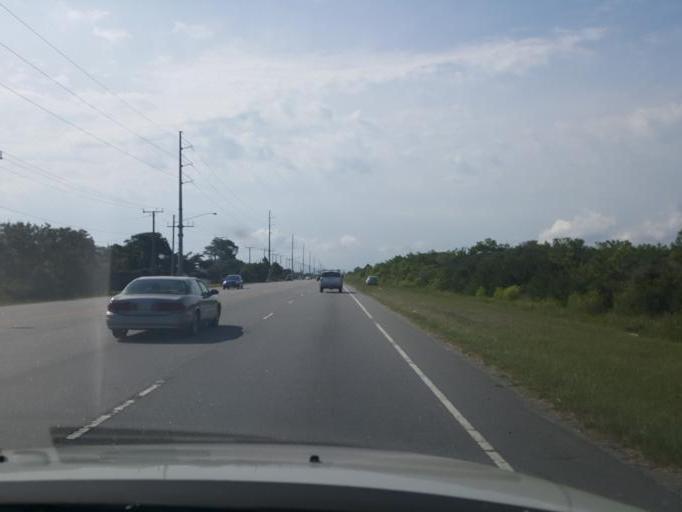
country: US
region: North Carolina
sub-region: Dare County
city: Kill Devil Hills
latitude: 36.0194
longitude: -75.6645
